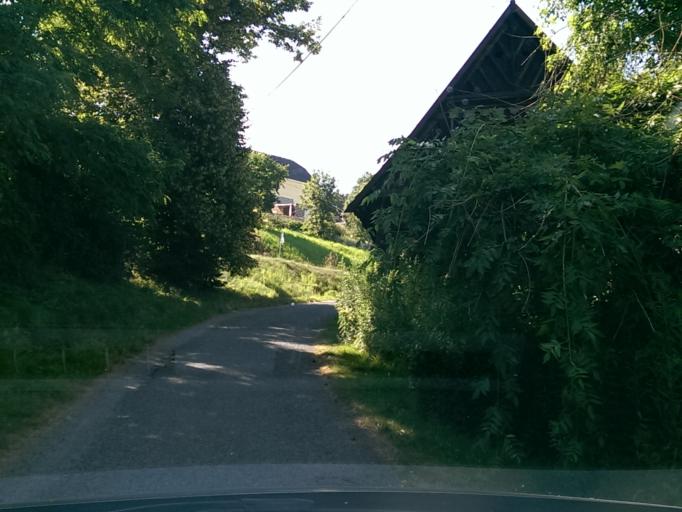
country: CZ
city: Duba
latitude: 50.5441
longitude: 14.4927
